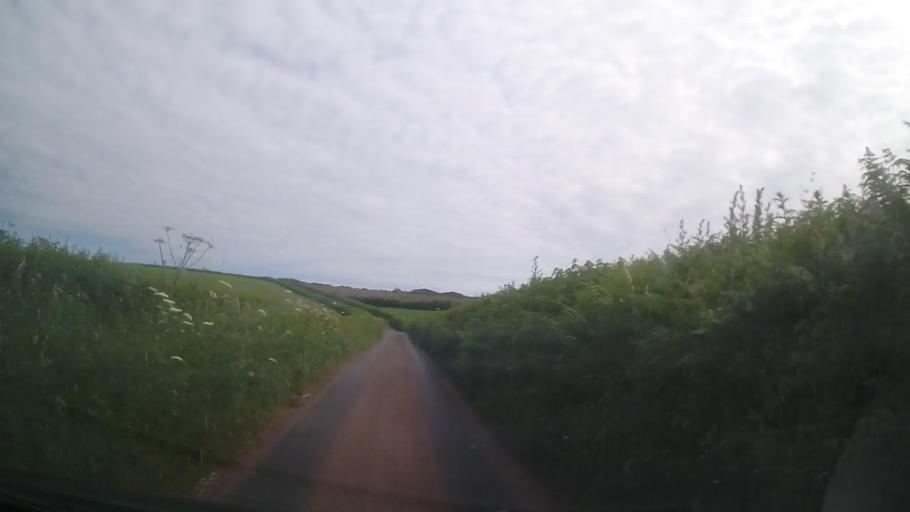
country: GB
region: England
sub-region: Devon
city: Salcombe
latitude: 50.2367
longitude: -3.6744
